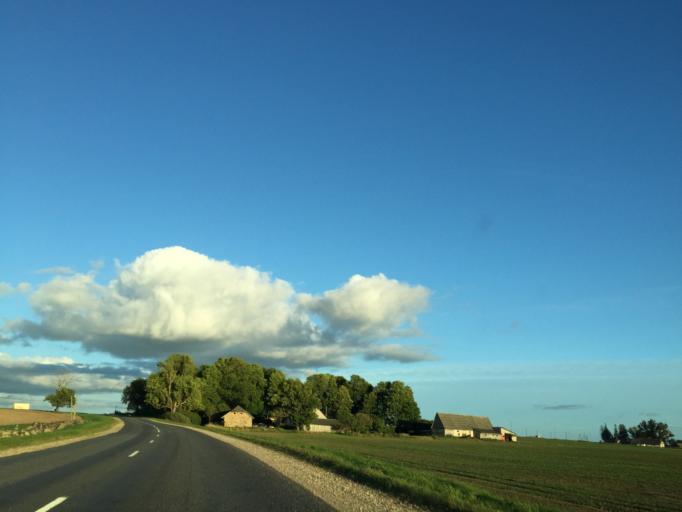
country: LV
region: Saldus Rajons
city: Saldus
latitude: 56.7134
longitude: 22.4016
